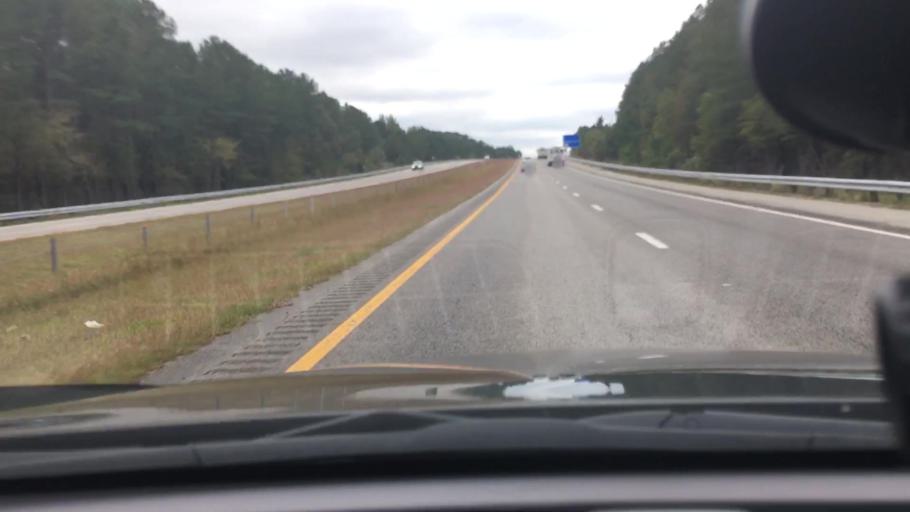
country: US
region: North Carolina
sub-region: Wilson County
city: Wilson
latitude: 35.6711
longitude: -77.8671
